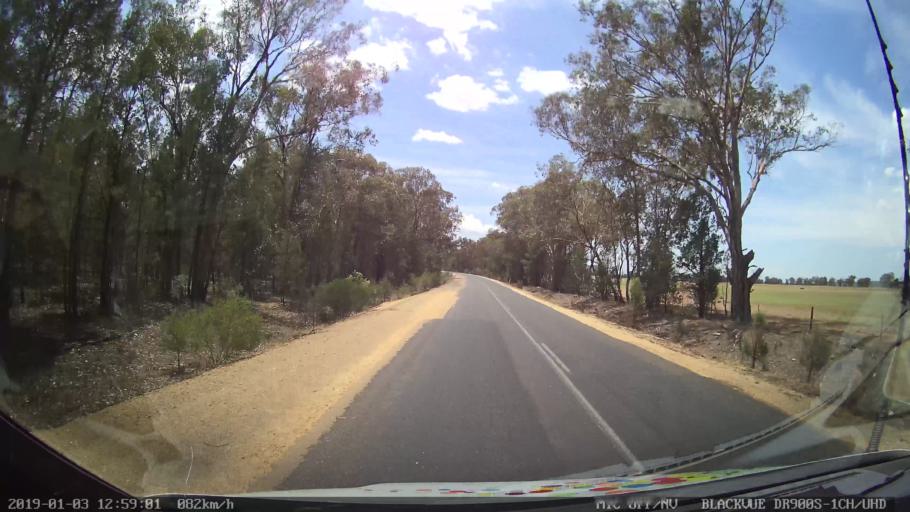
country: AU
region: New South Wales
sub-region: Cabonne
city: Canowindra
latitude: -33.6394
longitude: 148.3835
